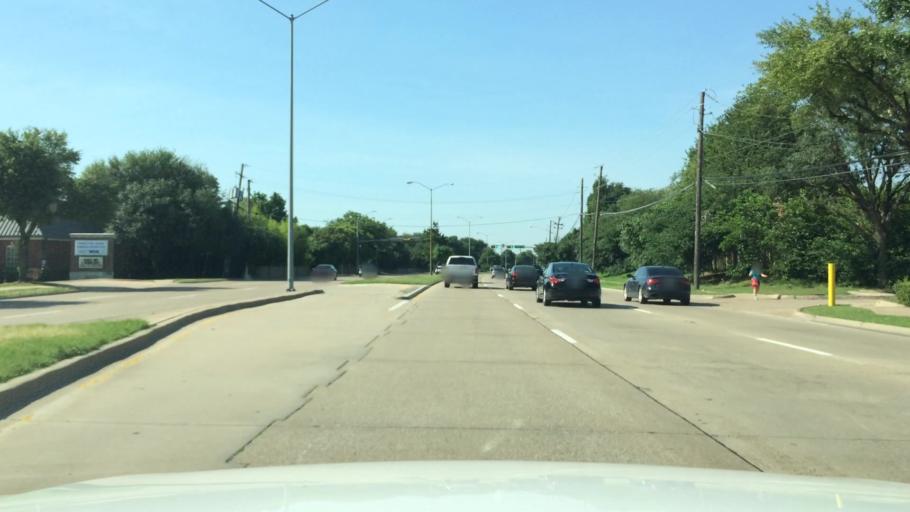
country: US
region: Texas
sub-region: Dallas County
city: Addison
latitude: 33.0061
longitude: -96.7956
